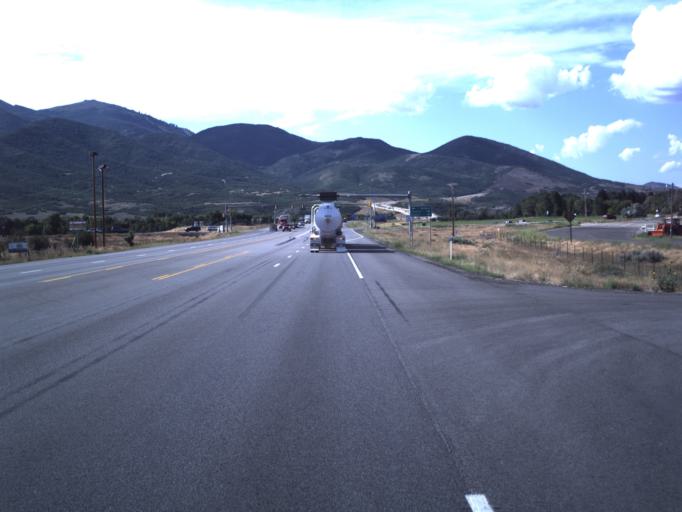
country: US
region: Utah
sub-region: Wasatch County
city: Heber
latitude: 40.5555
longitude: -111.4243
